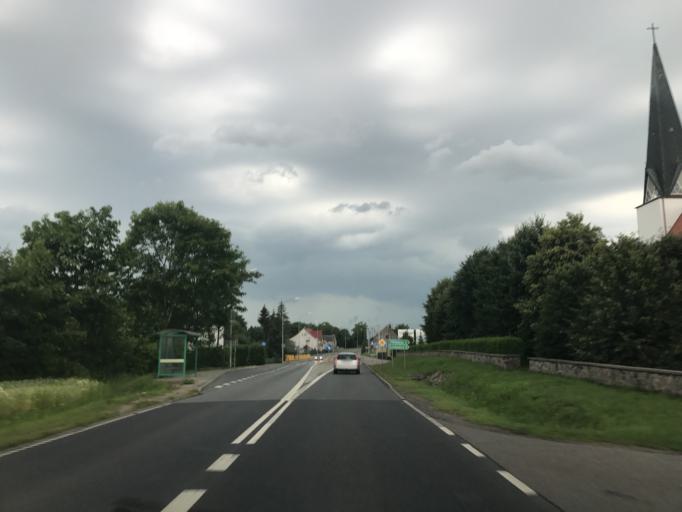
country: PL
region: Kujawsko-Pomorskie
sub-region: Powiat tucholski
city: Kesowo
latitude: 53.6454
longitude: 17.7117
